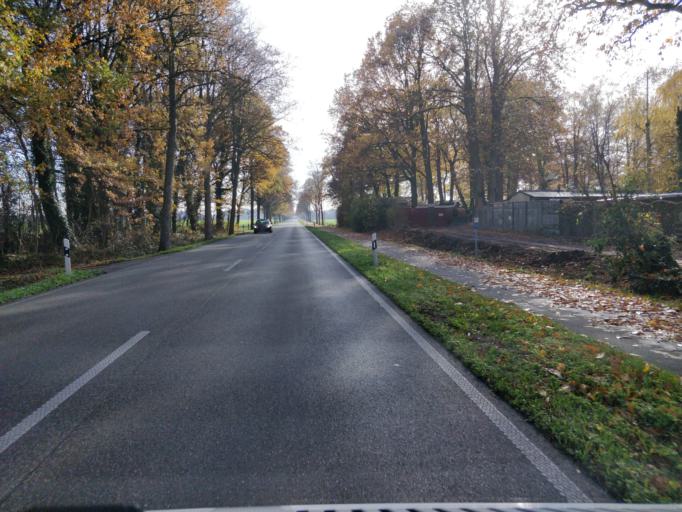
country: DE
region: North Rhine-Westphalia
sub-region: Regierungsbezirk Dusseldorf
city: Mehrhoog
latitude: 51.7463
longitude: 6.4915
